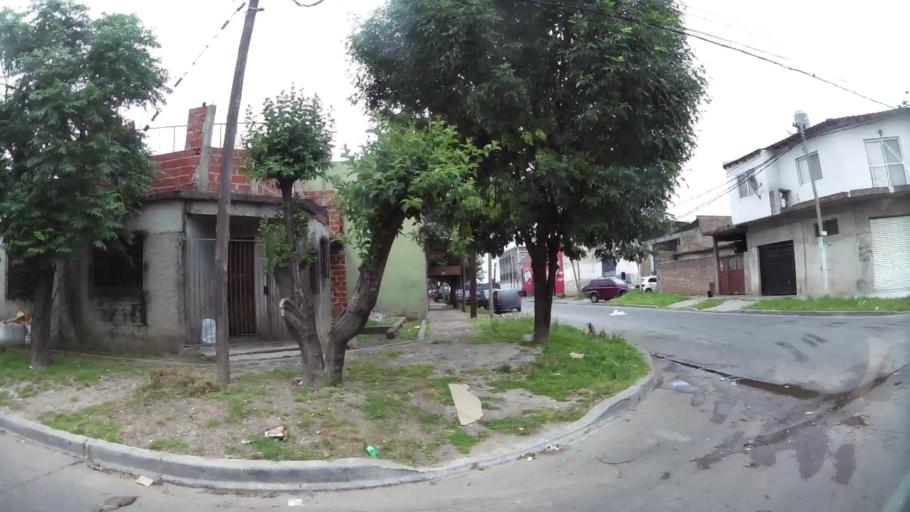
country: AR
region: Buenos Aires
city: San Justo
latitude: -34.7075
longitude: -58.5530
